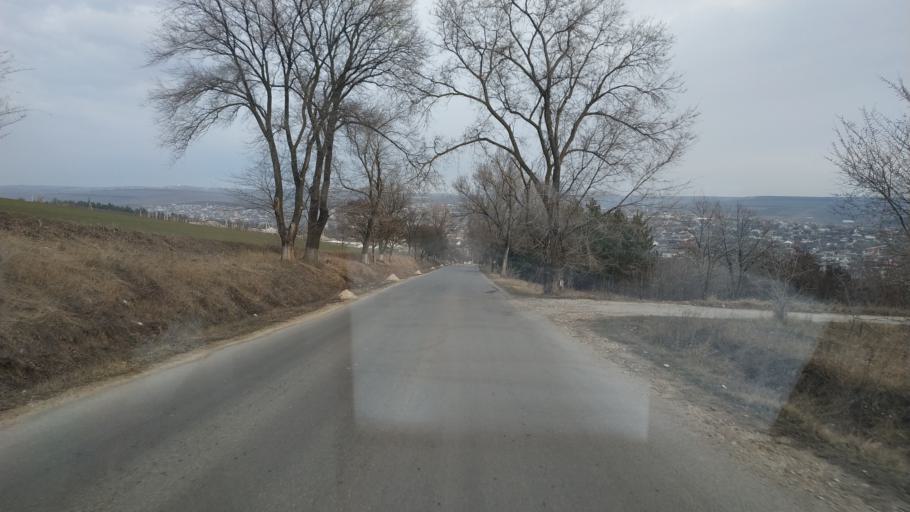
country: MD
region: Chisinau
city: Singera
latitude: 46.9513
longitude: 29.0576
